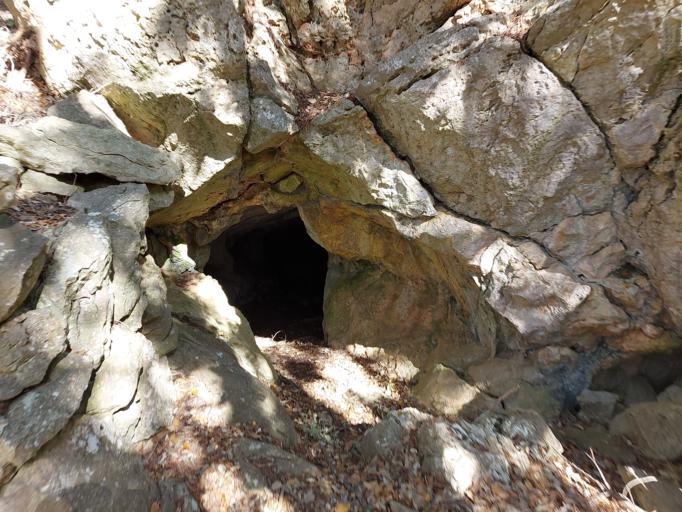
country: ES
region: Balearic Islands
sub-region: Illes Balears
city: Mancor de la Vall
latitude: 39.7464
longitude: 2.8426
